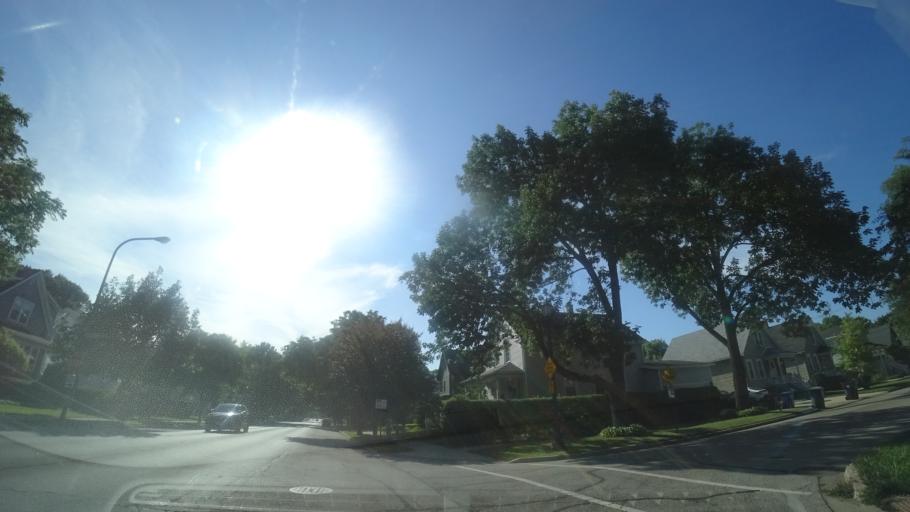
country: US
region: Illinois
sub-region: Cook County
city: Evanston
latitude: 42.0442
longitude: -87.6948
